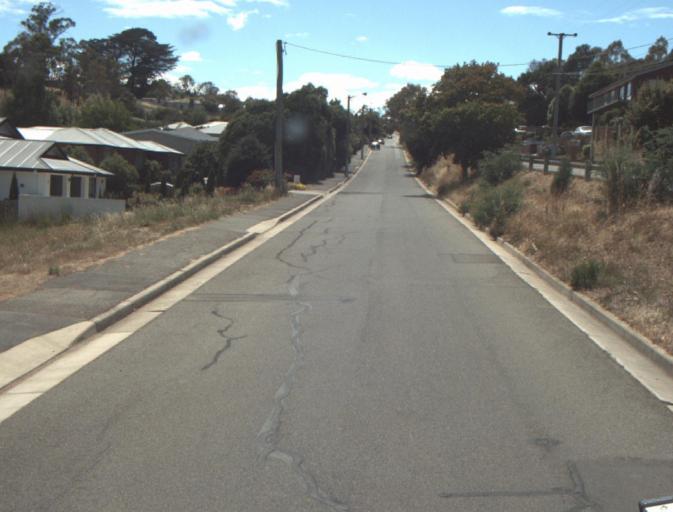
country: AU
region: Tasmania
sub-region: Launceston
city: Summerhill
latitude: -41.4624
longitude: 147.1242
